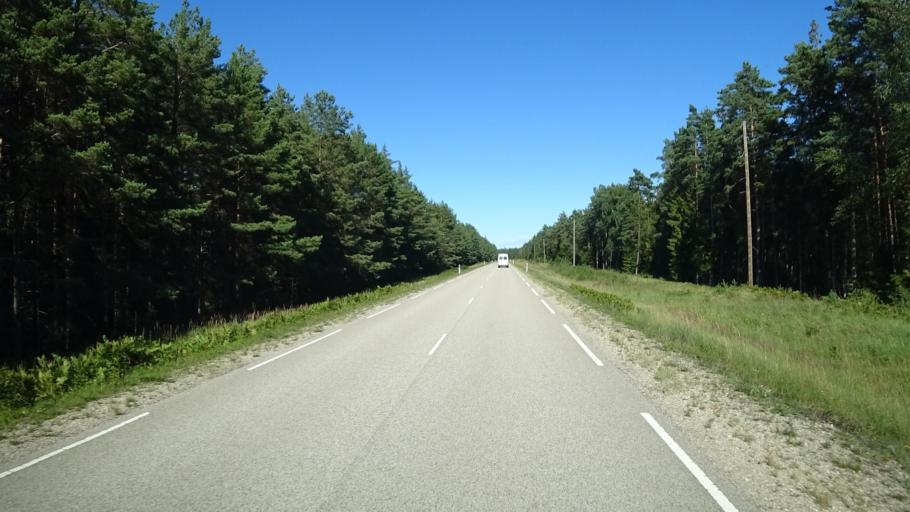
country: LV
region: Dundaga
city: Dundaga
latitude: 57.7311
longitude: 22.5115
